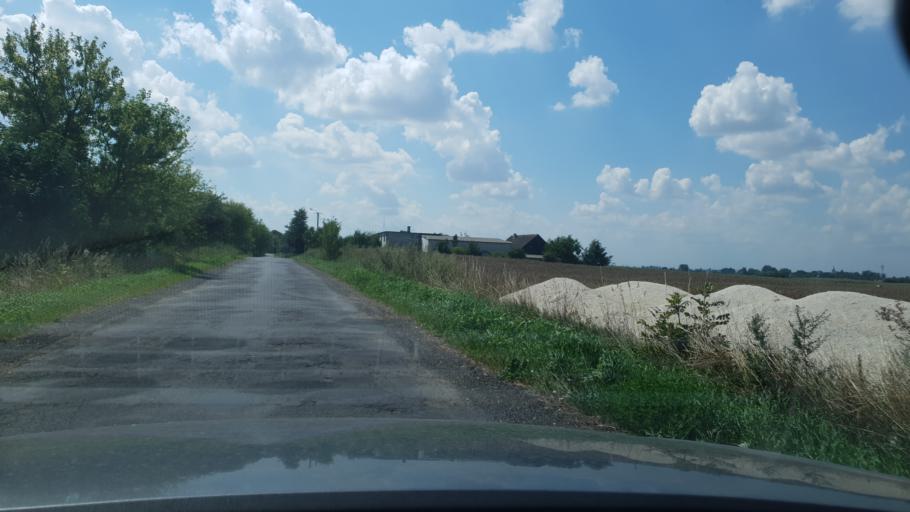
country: PL
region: Kujawsko-Pomorskie
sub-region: Powiat wabrzeski
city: Pluznica
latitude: 53.2991
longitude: 18.8048
